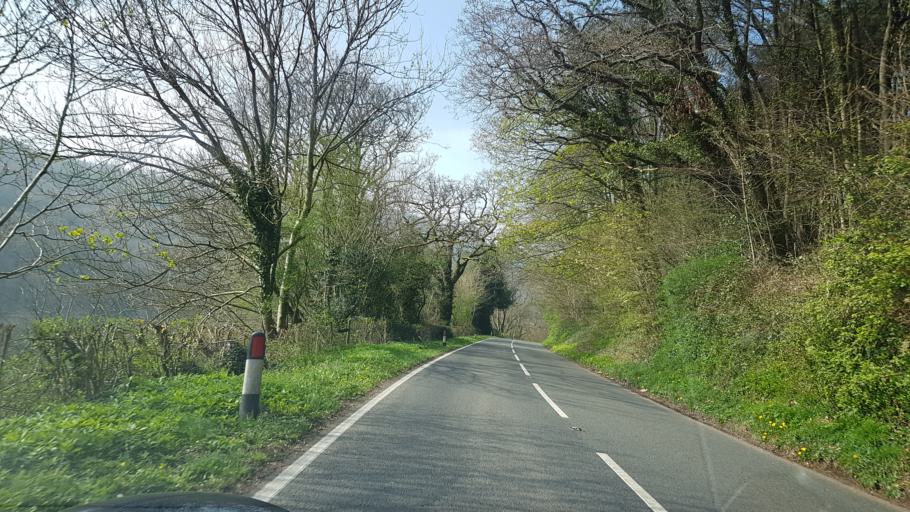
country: GB
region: Wales
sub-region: Monmouthshire
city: Tintern
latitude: 51.7596
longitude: -2.6687
